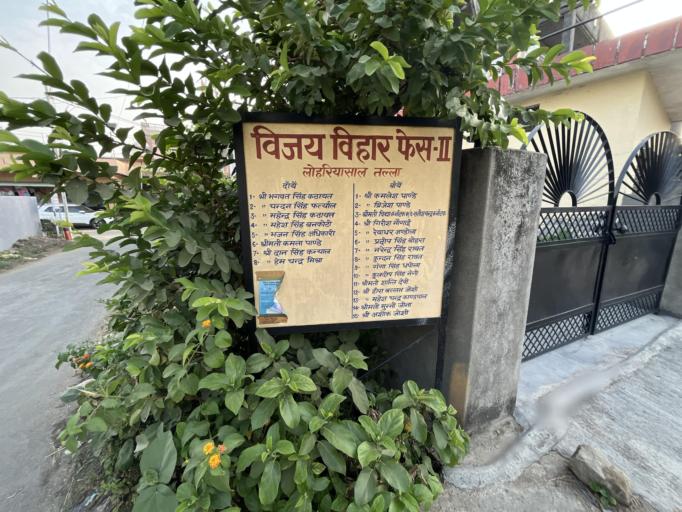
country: IN
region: Uttarakhand
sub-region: Naini Tal
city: Haldwani
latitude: 29.2246
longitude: 79.4882
